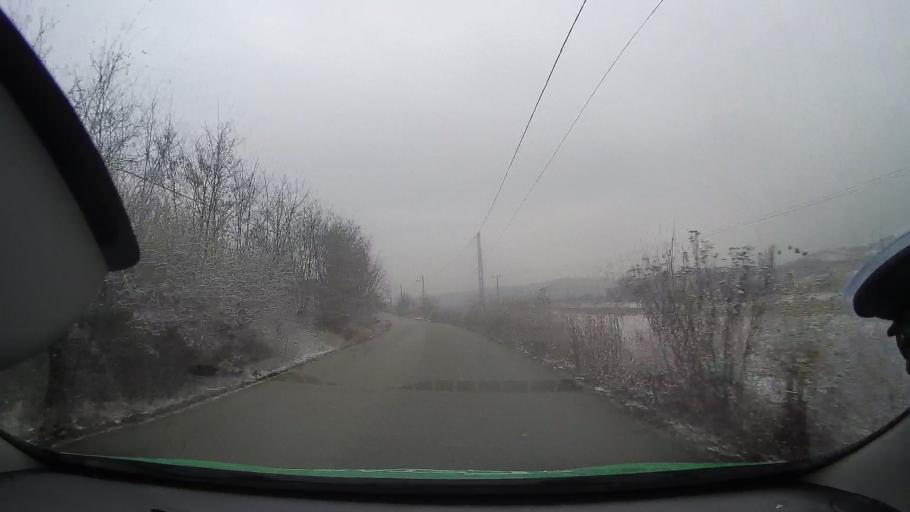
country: RO
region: Alba
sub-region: Comuna Noslac
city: Noslac
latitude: 46.3410
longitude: 23.9471
